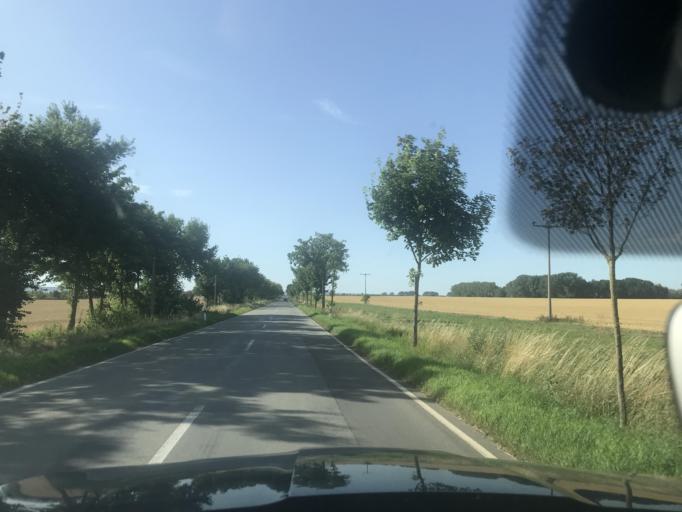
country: DE
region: Saxony-Anhalt
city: Wegeleben
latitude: 51.8925
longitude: 11.1630
